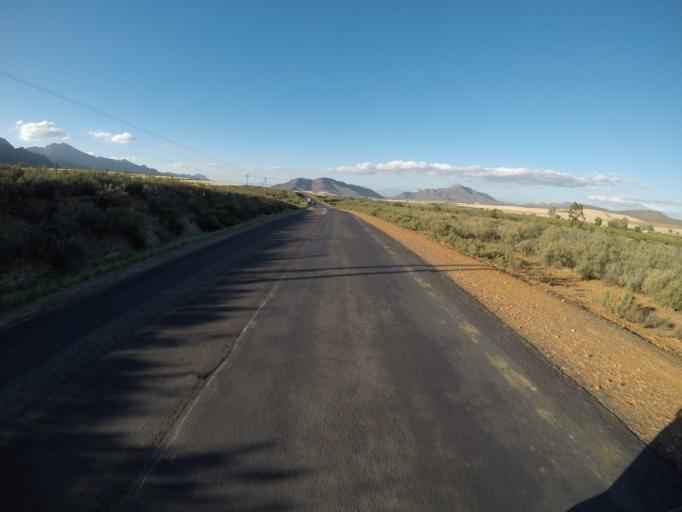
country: ZA
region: Western Cape
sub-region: Cape Winelands District Municipality
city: Worcester
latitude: -33.9138
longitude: 19.3625
